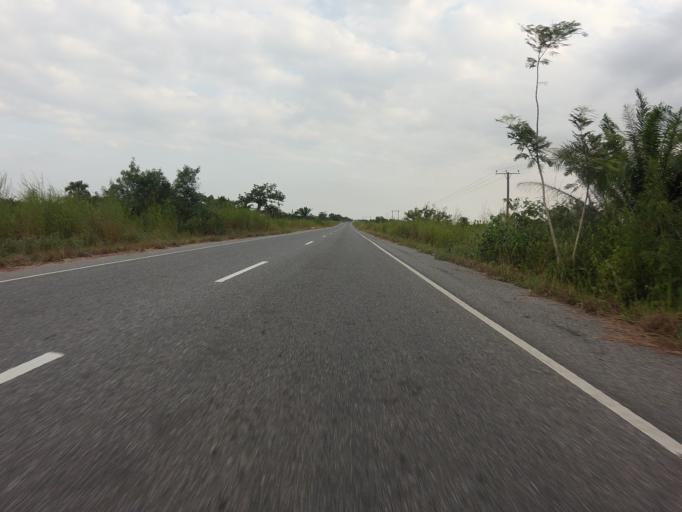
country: GH
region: Volta
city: Ho
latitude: 6.2459
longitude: 0.5508
